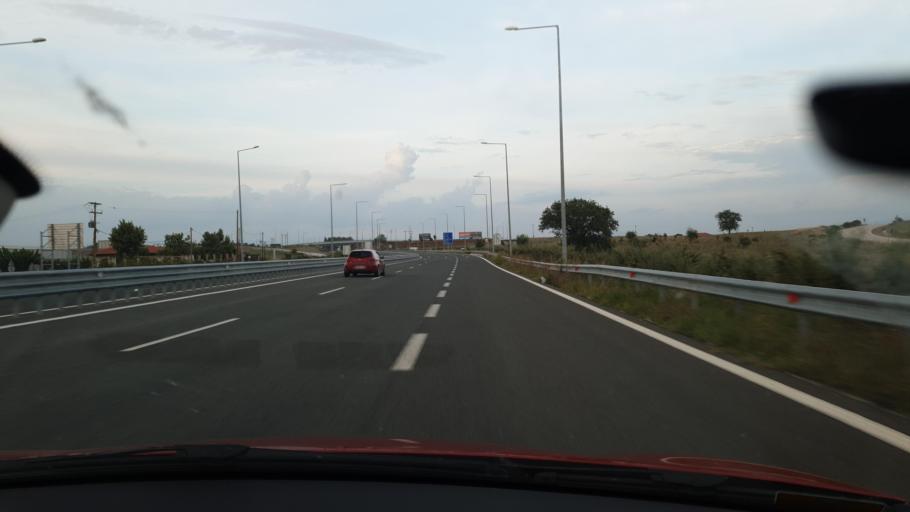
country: GR
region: Central Macedonia
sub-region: Nomos Kilkis
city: Kristoni
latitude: 40.9562
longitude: 22.8490
